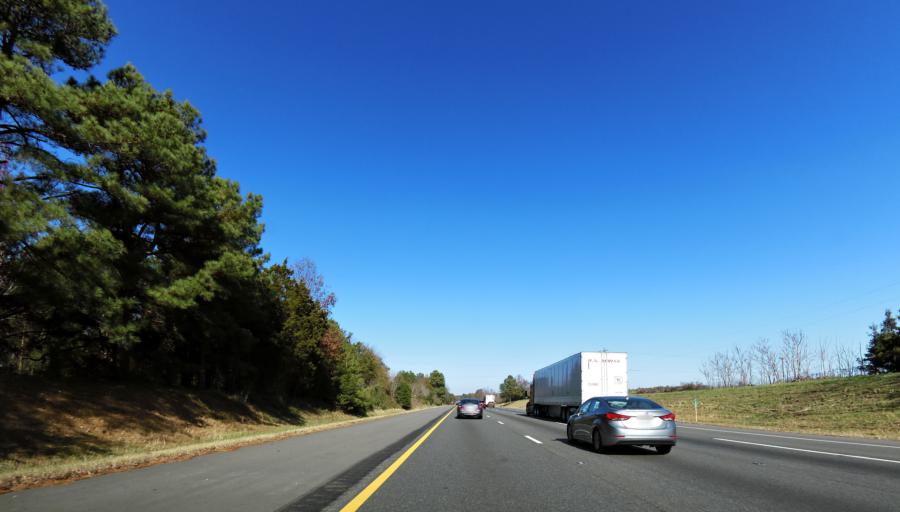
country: US
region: Virginia
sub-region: Caroline County
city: Bowling Green
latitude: 38.0216
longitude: -77.4990
